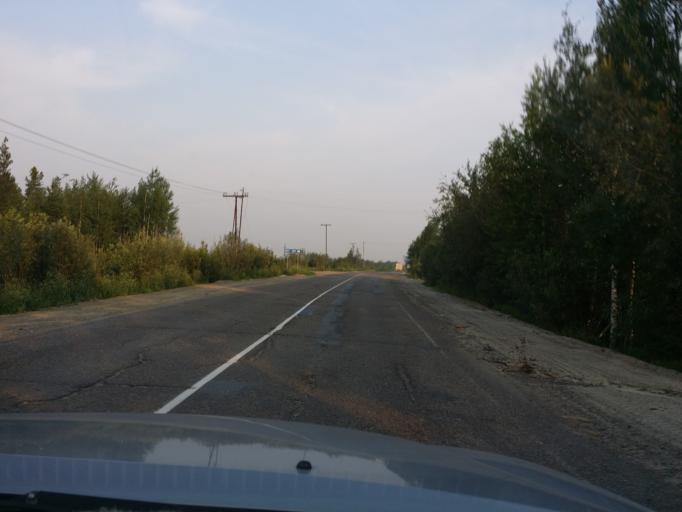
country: RU
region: Khanty-Mansiyskiy Avtonomnyy Okrug
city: Nizhnevartovsk
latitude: 61.1932
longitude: 76.5535
